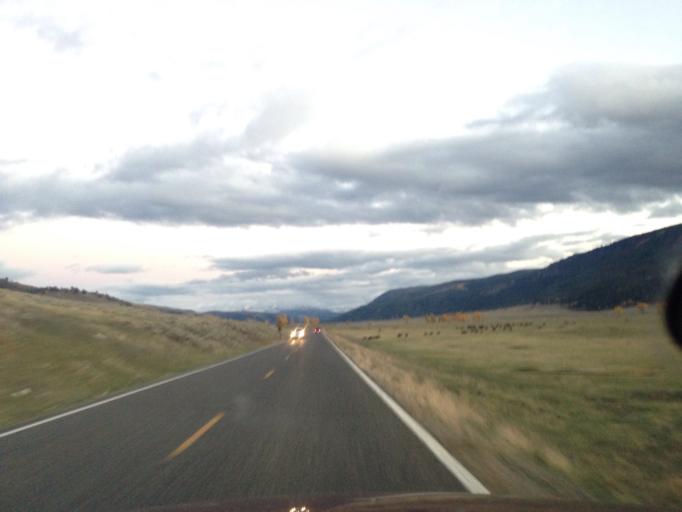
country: US
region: Montana
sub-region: Park County
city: Livingston
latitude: 44.9004
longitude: -110.2417
